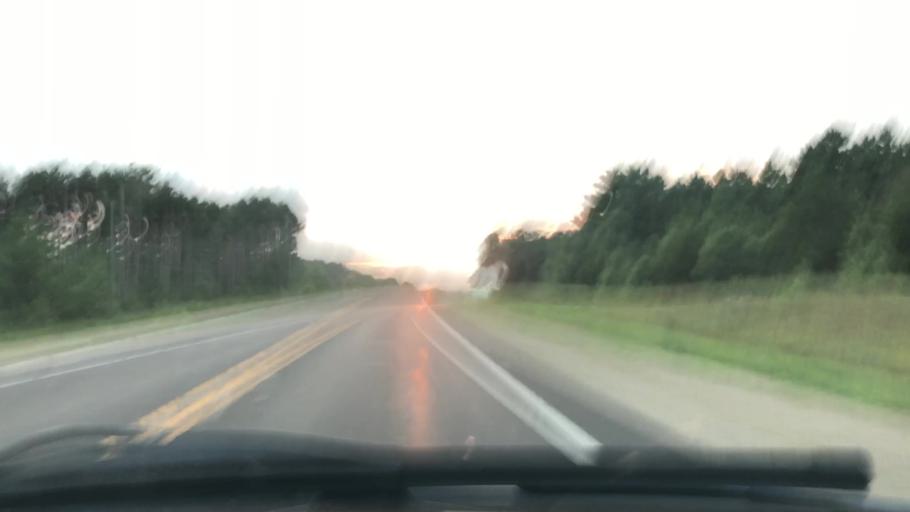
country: US
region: Wisconsin
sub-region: Sauk County
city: Spring Green
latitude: 43.1926
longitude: -90.2236
